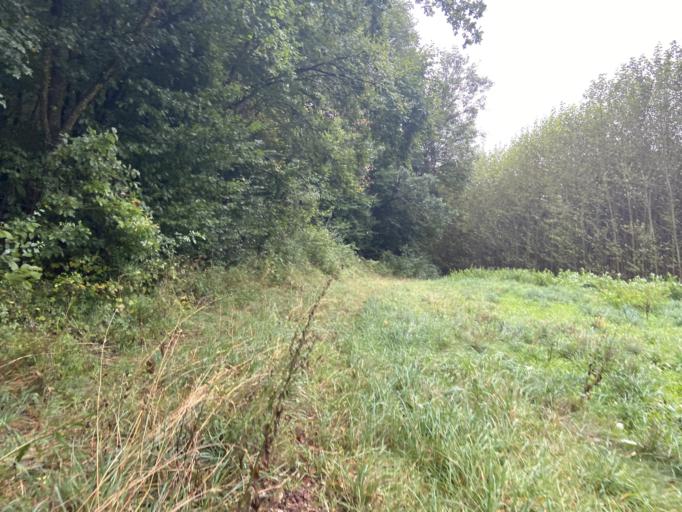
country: DE
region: Baden-Wuerttemberg
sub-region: Tuebingen Region
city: Bingen
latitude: 48.1157
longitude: 9.2531
